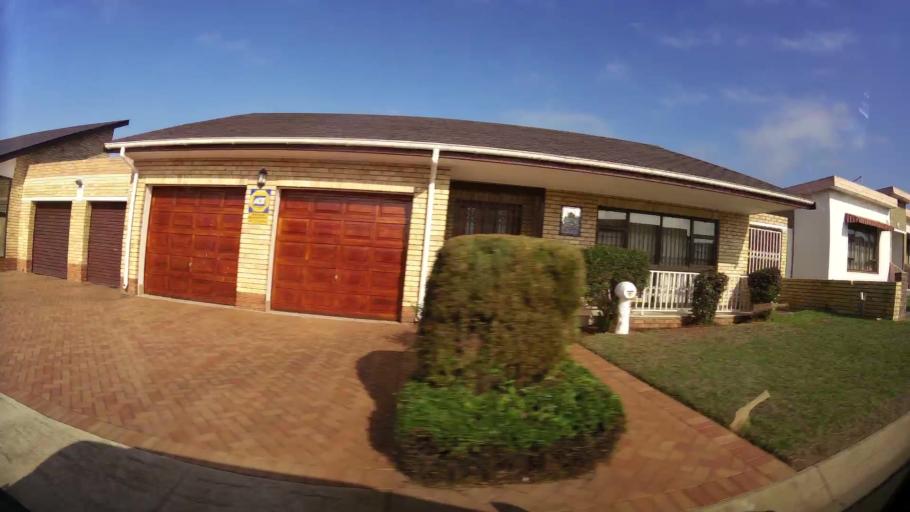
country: ZA
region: Eastern Cape
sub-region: Nelson Mandela Bay Metropolitan Municipality
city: Port Elizabeth
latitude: -33.9238
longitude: 25.5321
